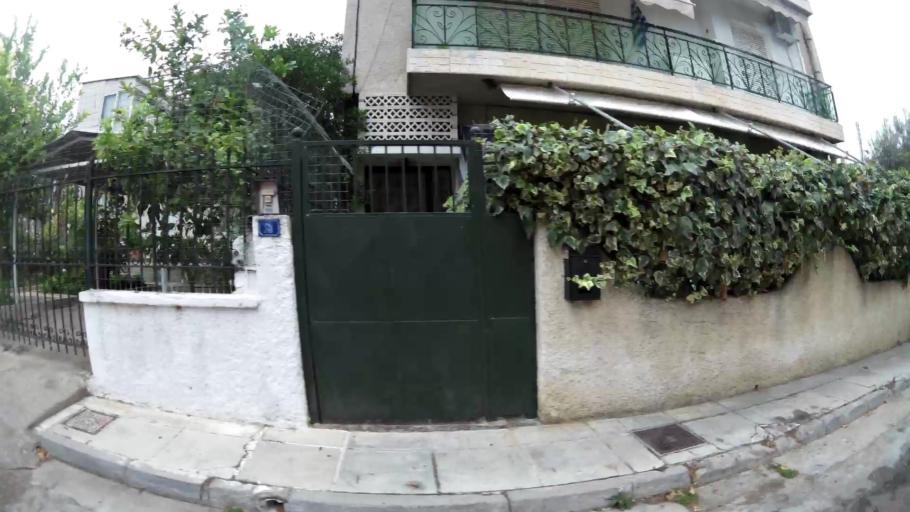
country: GR
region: Attica
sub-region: Nomarchia Athinas
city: Agioi Anargyroi
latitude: 38.0356
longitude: 23.7155
